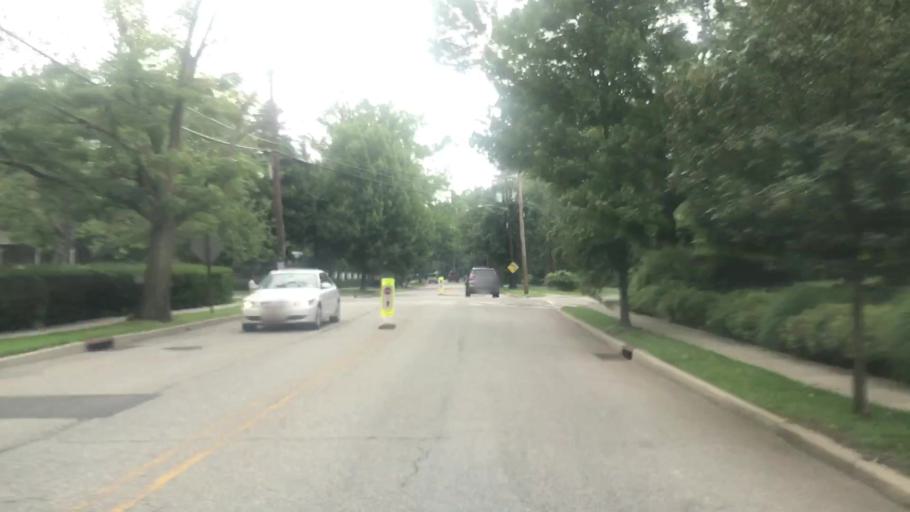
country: US
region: New Jersey
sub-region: Bergen County
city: Englewood
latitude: 40.8850
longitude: -73.9704
